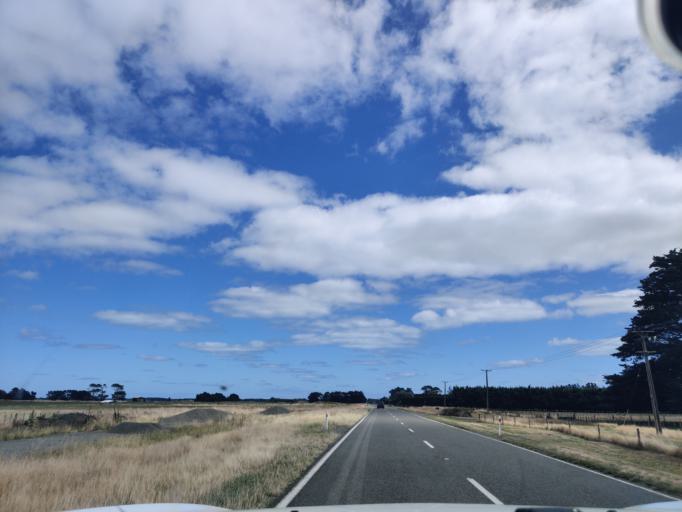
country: NZ
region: Manawatu-Wanganui
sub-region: Horowhenua District
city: Foxton
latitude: -40.3946
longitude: 175.3313
